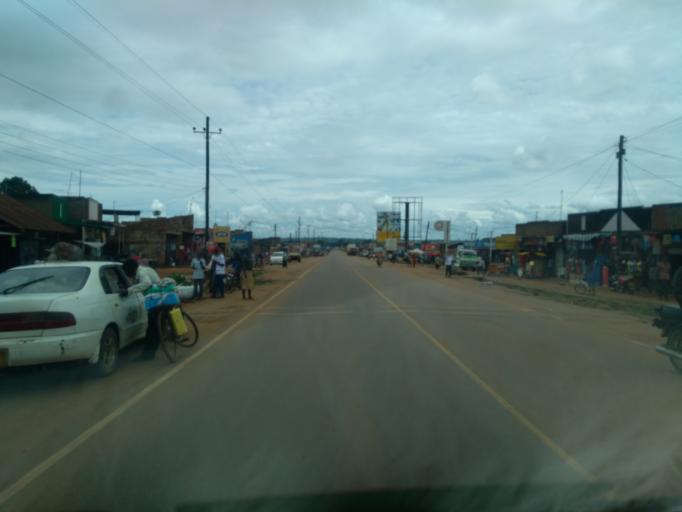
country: UG
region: Central Region
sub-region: Butambala District
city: Gombe
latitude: -0.0113
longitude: 32.0321
